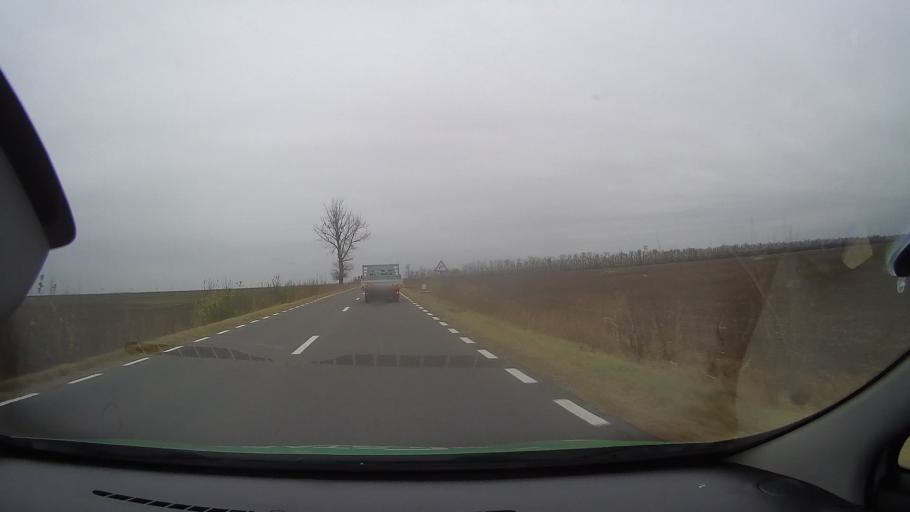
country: RO
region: Ialomita
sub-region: Comuna Gheorghe Lazar
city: Gheorghe Lazar
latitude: 44.6756
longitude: 27.4185
